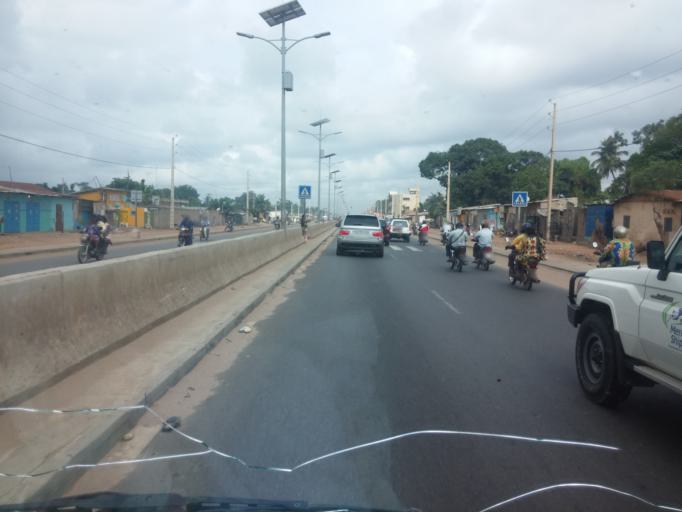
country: BJ
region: Atlantique
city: Hevie
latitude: 6.3878
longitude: 2.2762
